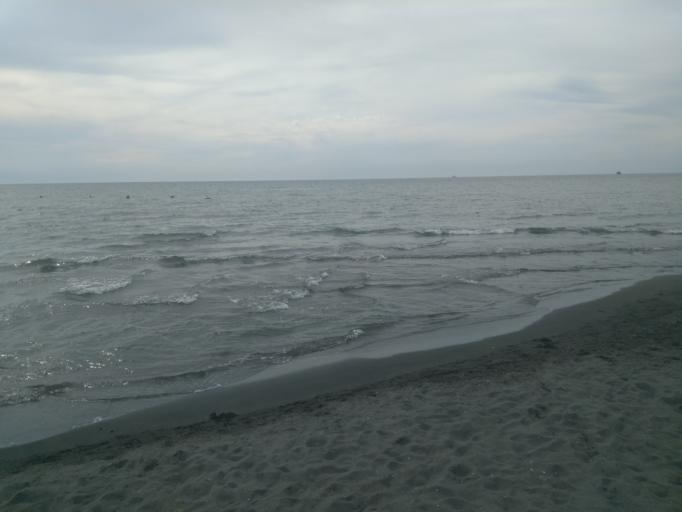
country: GE
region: Guria
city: Urek'i
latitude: 41.9984
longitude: 41.7578
